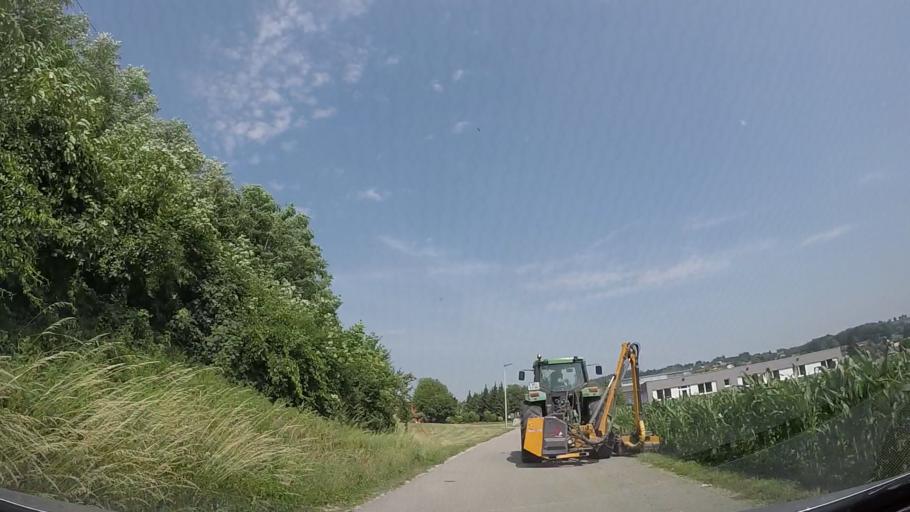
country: AT
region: Upper Austria
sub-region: Politischer Bezirk Grieskirchen
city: Bad Schallerbach
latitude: 48.2261
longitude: 13.9360
